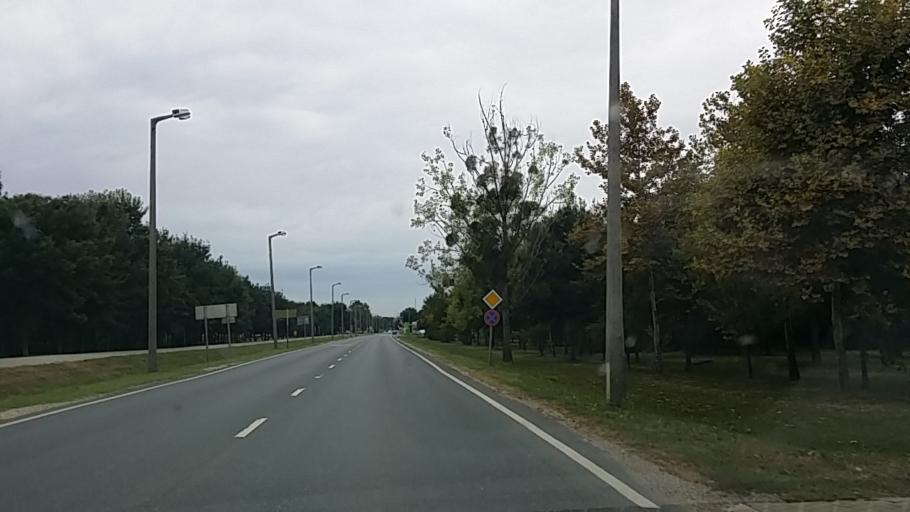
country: HU
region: Gyor-Moson-Sopron
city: Kapuvar
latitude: 47.5916
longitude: 17.0393
